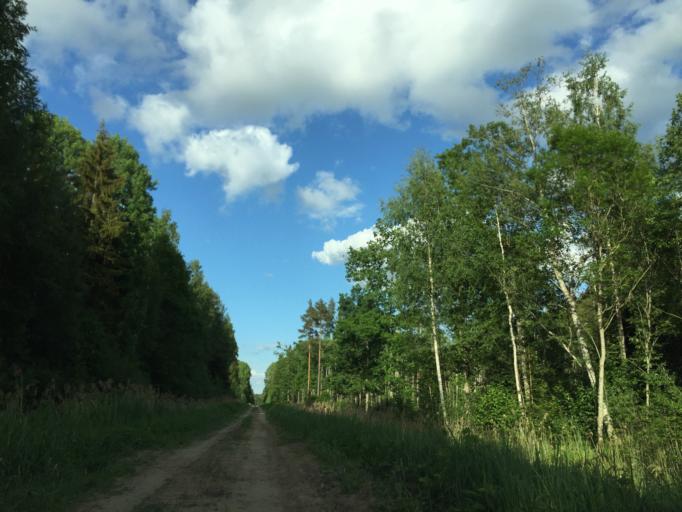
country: LV
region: Engure
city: Smarde
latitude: 56.7772
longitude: 23.4049
